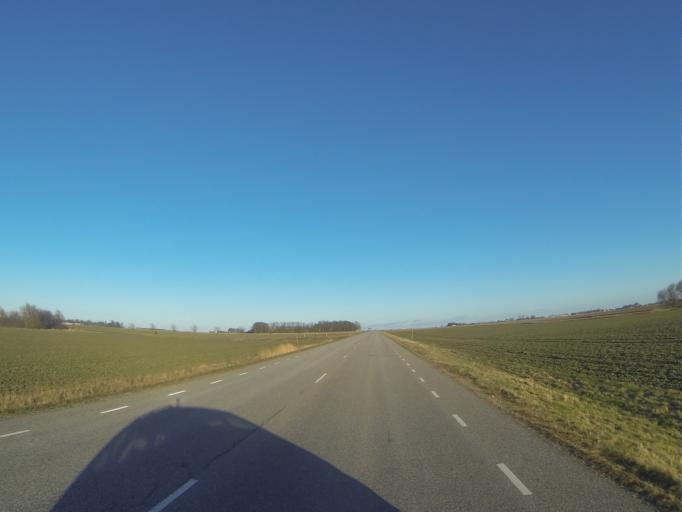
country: SE
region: Skane
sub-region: Malmo
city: Tygelsjo
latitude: 55.5444
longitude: 12.9880
